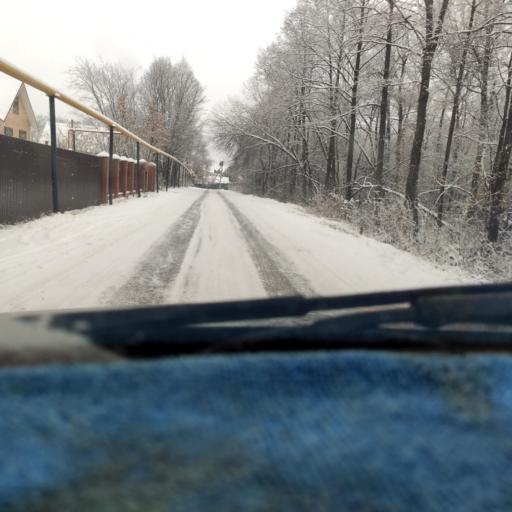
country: RU
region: Bashkortostan
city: Avdon
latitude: 54.6746
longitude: 55.8499
